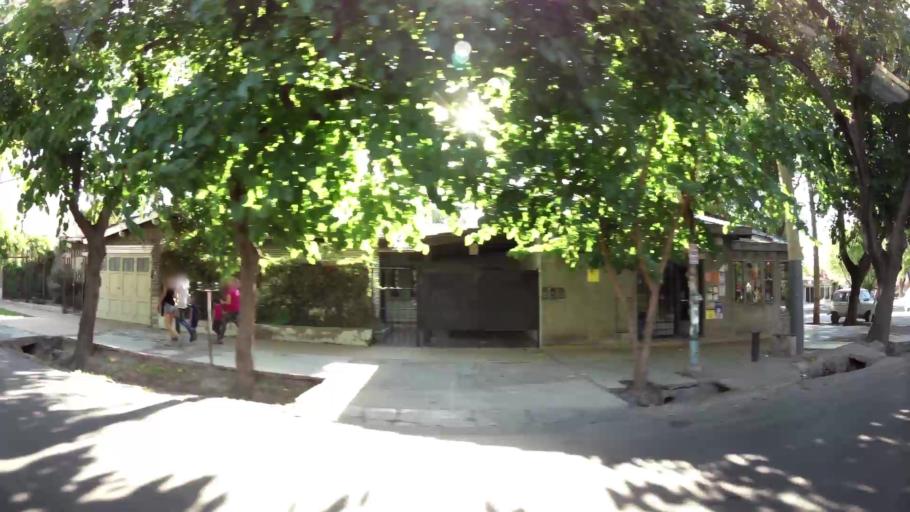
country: AR
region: Mendoza
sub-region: Departamento de Godoy Cruz
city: Godoy Cruz
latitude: -32.9104
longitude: -68.8294
